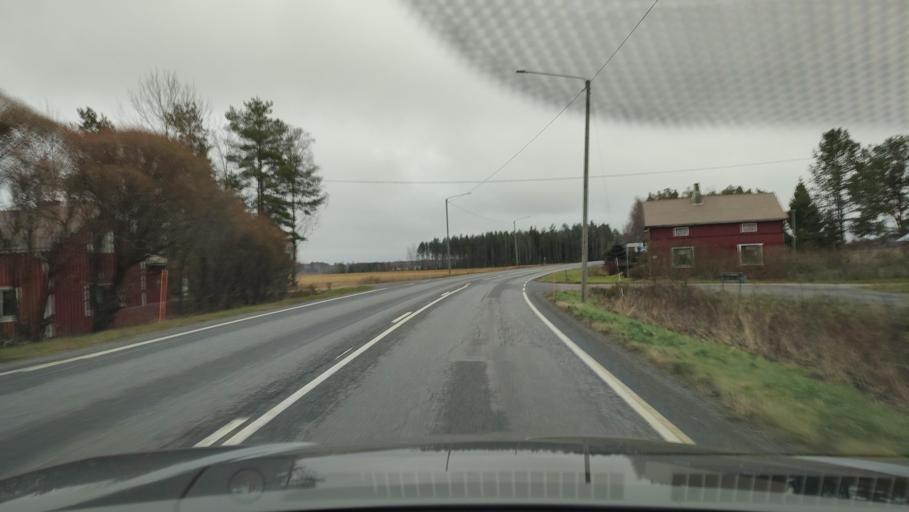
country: FI
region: Southern Ostrobothnia
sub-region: Suupohja
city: Isojoki
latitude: 62.1806
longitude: 21.8306
